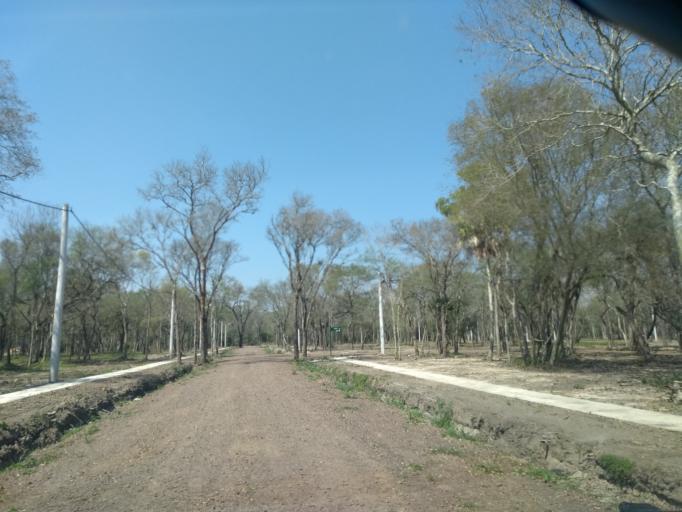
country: AR
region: Chaco
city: Resistencia
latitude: -27.4110
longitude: -58.9557
